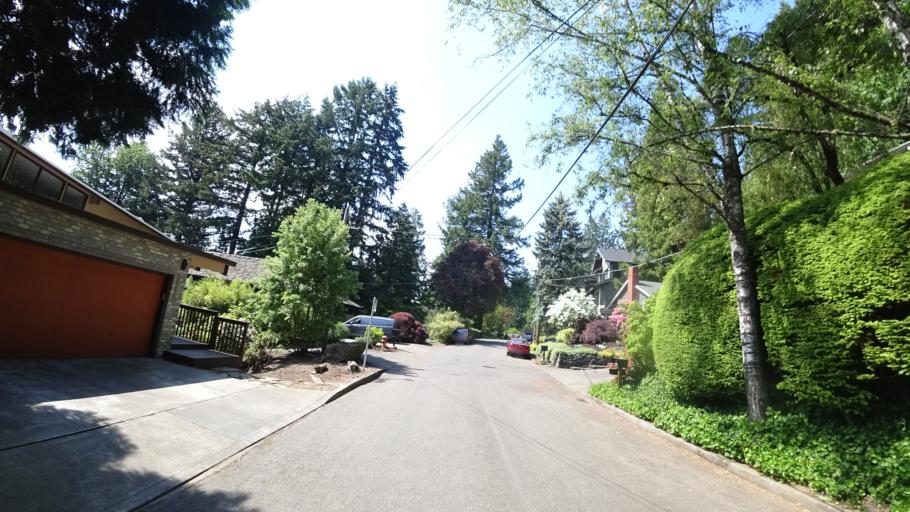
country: US
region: Oregon
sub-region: Multnomah County
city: Portland
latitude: 45.4922
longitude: -122.7041
